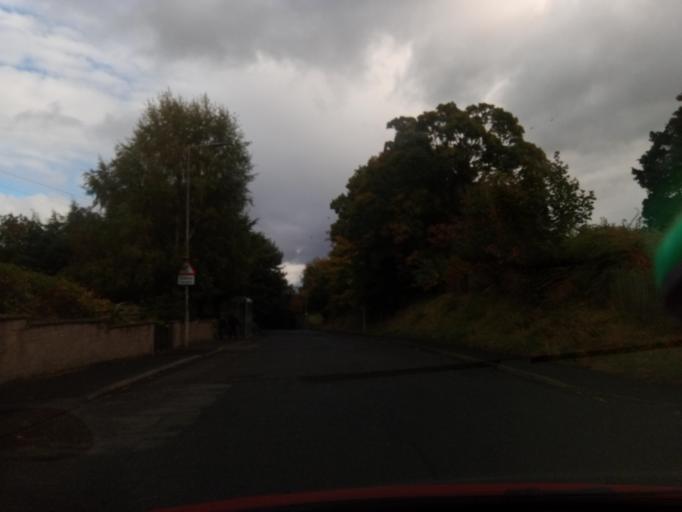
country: GB
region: Scotland
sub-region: The Scottish Borders
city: Galashiels
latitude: 55.6073
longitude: -2.7866
